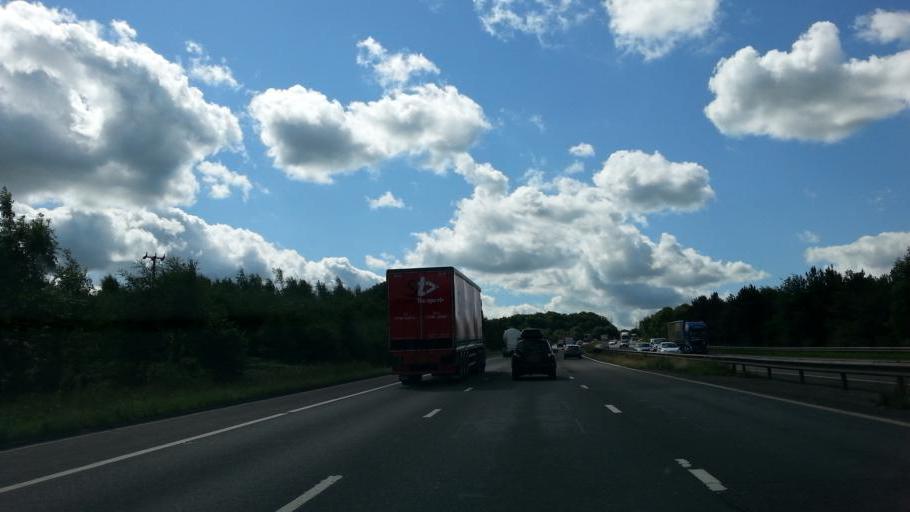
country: GB
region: England
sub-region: Leicestershire
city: Shepshed
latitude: 52.7295
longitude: -1.2823
